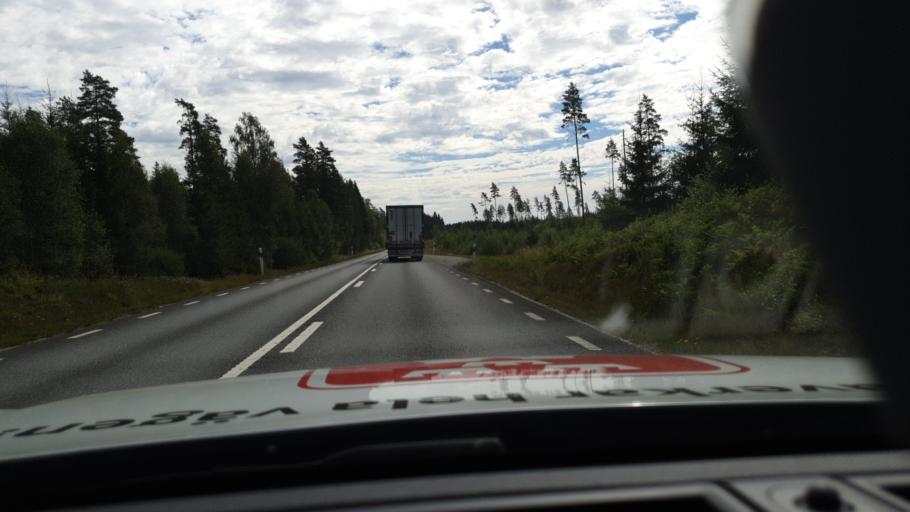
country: SE
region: Joenkoeping
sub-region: Savsjo Kommun
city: Vrigstad
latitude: 57.3750
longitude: 14.4092
